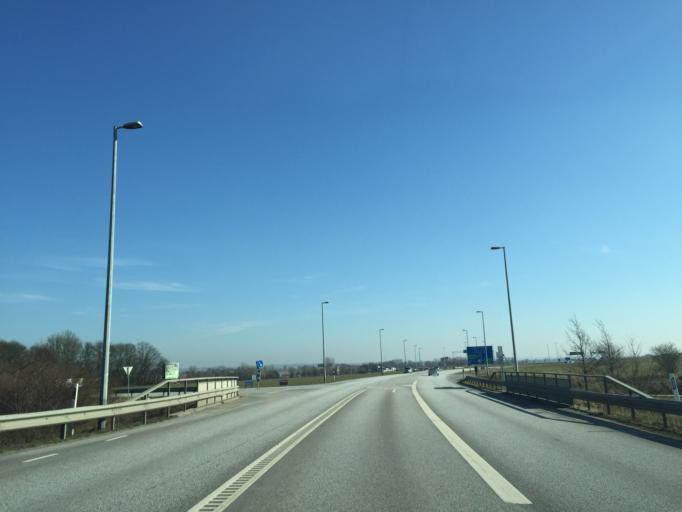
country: SE
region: Skane
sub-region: Lunds Kommun
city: Lund
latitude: 55.6805
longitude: 13.1749
